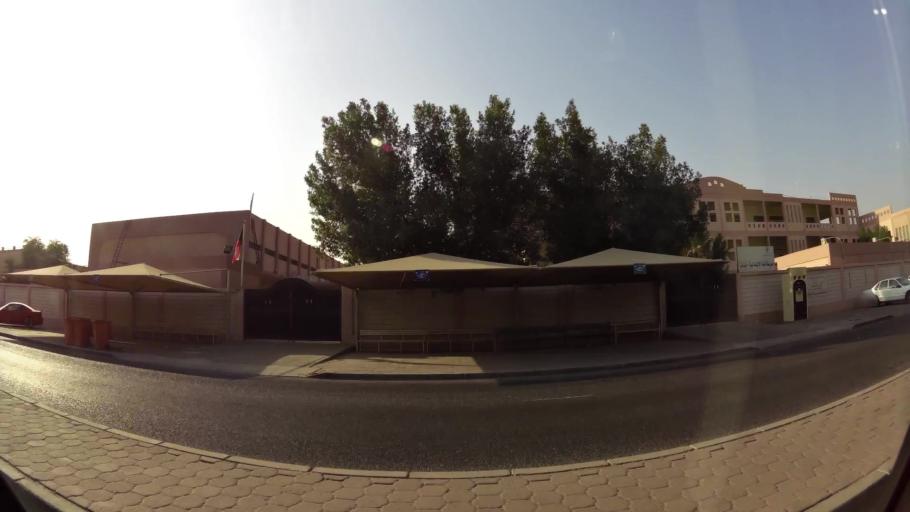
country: KW
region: Al Asimah
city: Ad Dasmah
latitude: 29.3687
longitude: 47.9985
